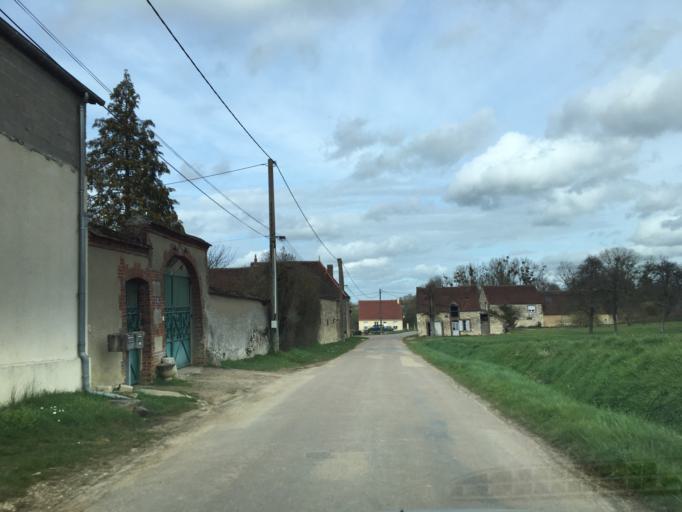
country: FR
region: Bourgogne
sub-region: Departement de l'Yonne
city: Fleury-la-Vallee
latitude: 47.8619
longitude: 3.4094
